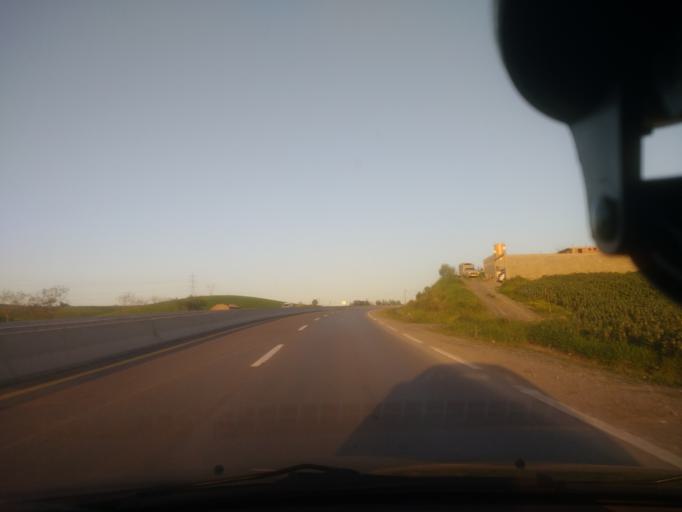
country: DZ
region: Boumerdes
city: Makouda
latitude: 36.7573
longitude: 4.0450
